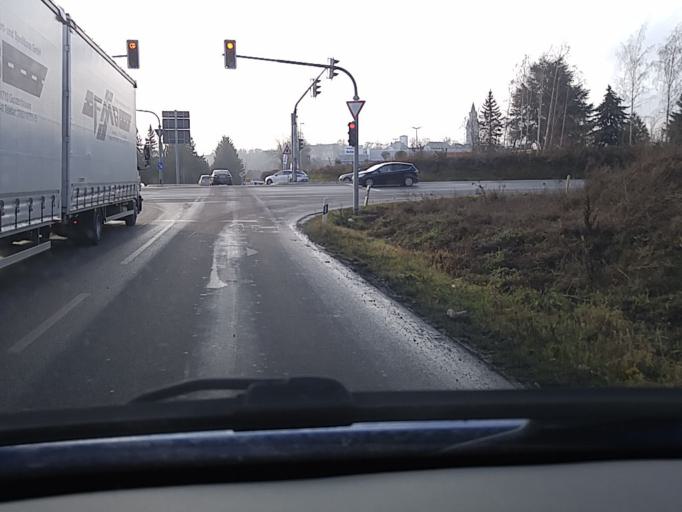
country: DE
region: Hesse
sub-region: Regierungsbezirk Darmstadt
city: Friedberg
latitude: 50.3478
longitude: 8.7588
